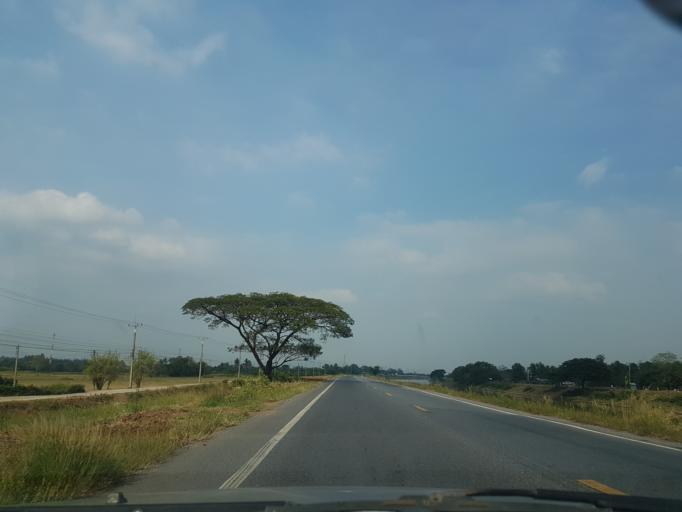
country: TH
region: Phra Nakhon Si Ayutthaya
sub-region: Amphoe Tha Ruea
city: Tha Ruea
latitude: 14.5234
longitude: 100.7397
